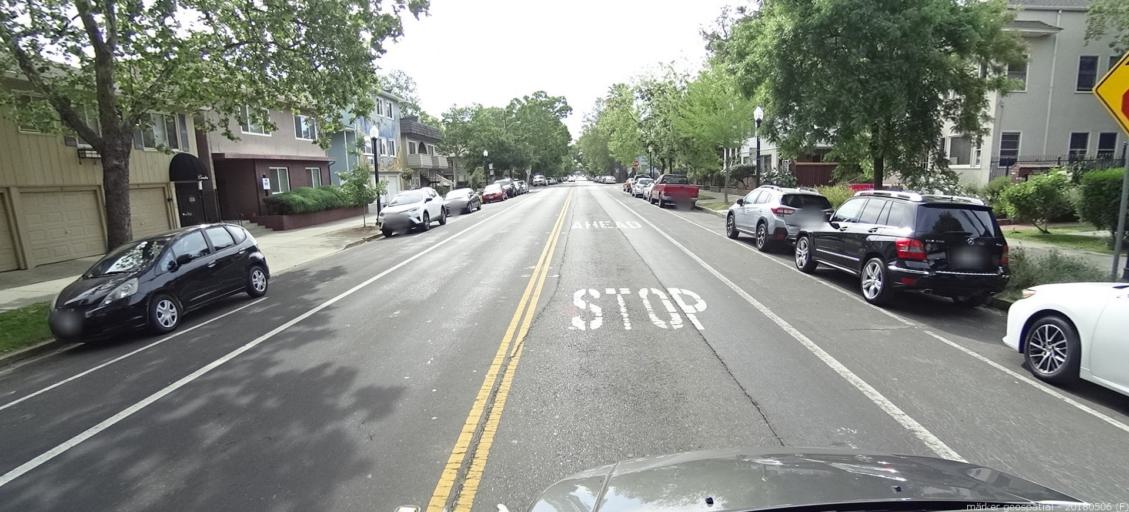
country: US
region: California
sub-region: Sacramento County
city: Sacramento
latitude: 38.5704
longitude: -121.4748
